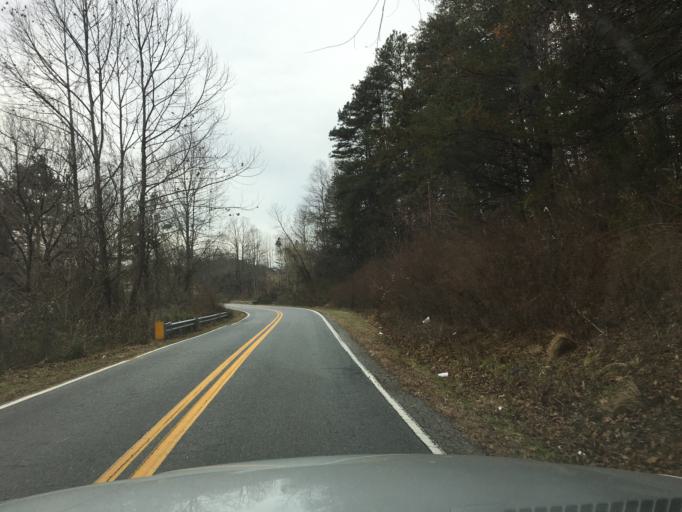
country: US
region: North Carolina
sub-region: McDowell County
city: West Marion
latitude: 35.6199
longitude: -81.9696
